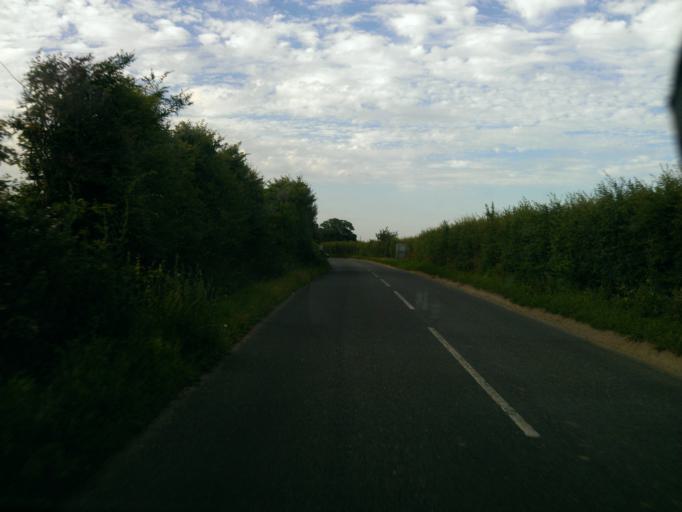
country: GB
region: England
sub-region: Essex
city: Great Bentley
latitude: 51.8606
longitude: 1.0656
